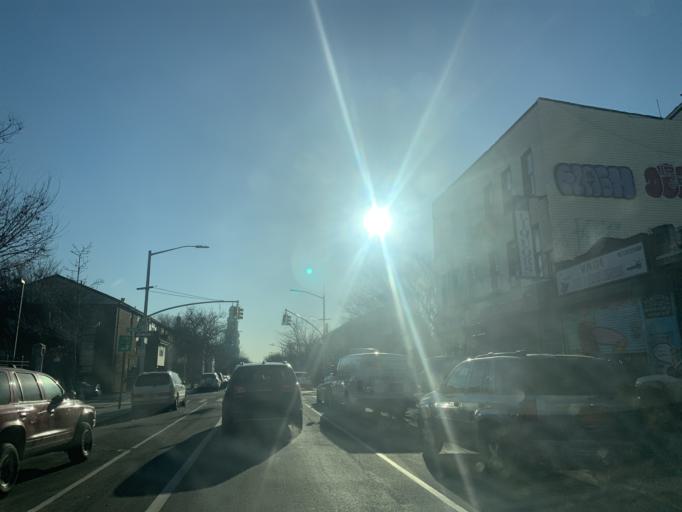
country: US
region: New York
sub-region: Kings County
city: East New York
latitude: 40.6971
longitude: -73.9234
